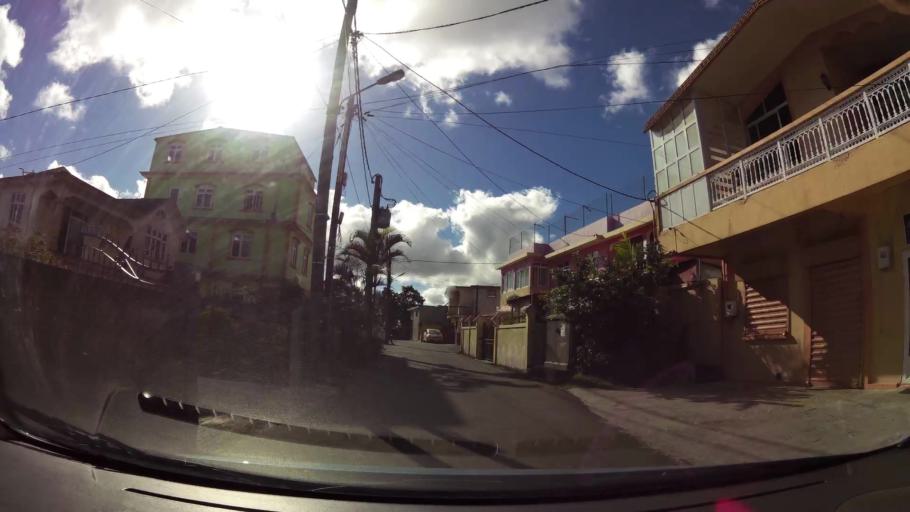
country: MU
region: Plaines Wilhems
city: Curepipe
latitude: -20.3026
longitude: 57.5182
